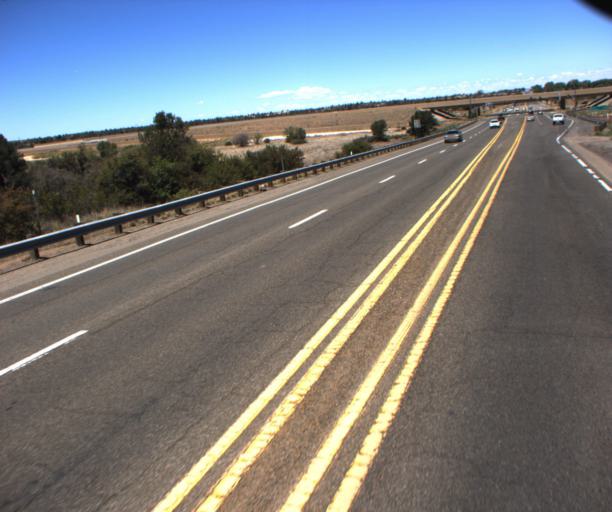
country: US
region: Arizona
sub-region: Yavapai County
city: Prescott
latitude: 34.6294
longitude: -112.4282
